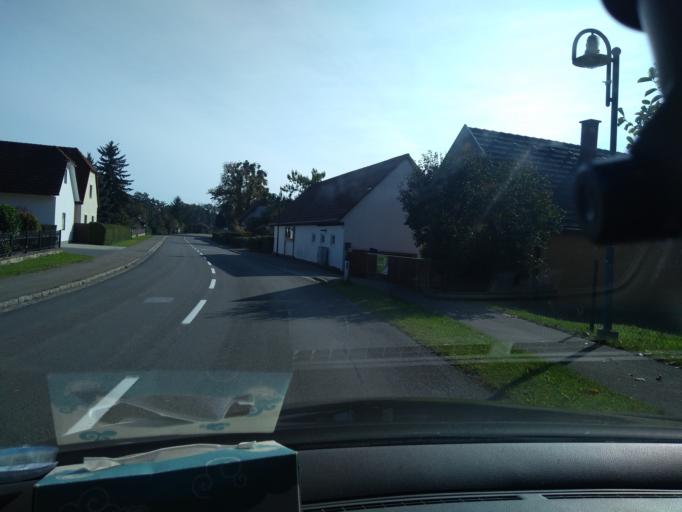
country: AT
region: Styria
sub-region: Politischer Bezirk Leibnitz
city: Stocking
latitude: 46.8510
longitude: 15.5367
